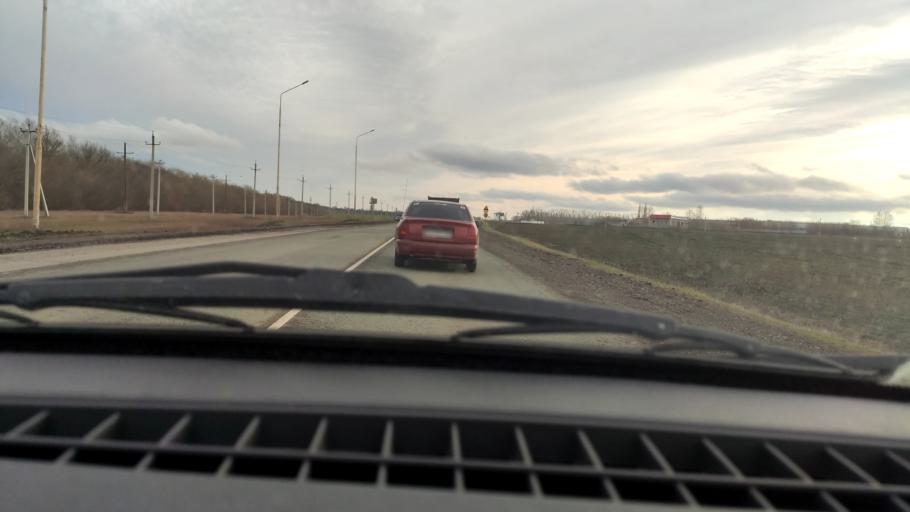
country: RU
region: Bashkortostan
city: Chishmy
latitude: 54.5714
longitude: 55.3551
